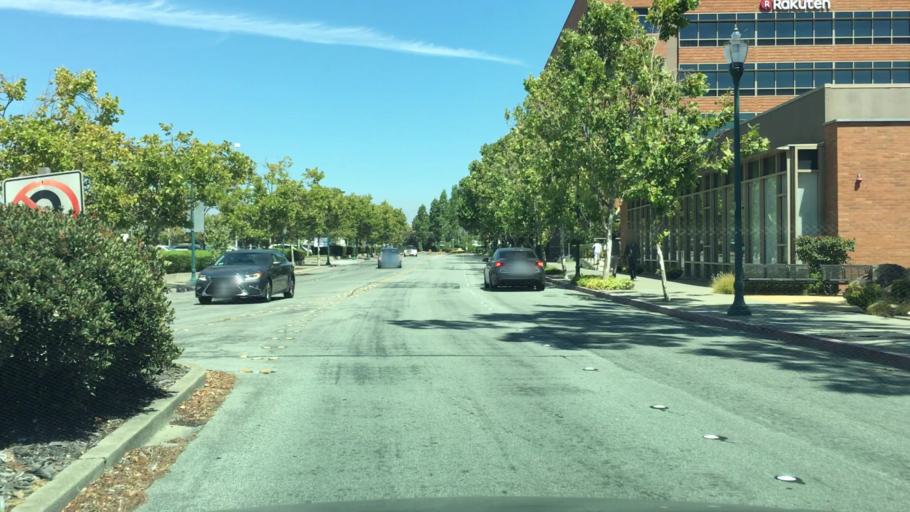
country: US
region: California
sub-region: San Mateo County
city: San Mateo
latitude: 37.5551
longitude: -122.3015
